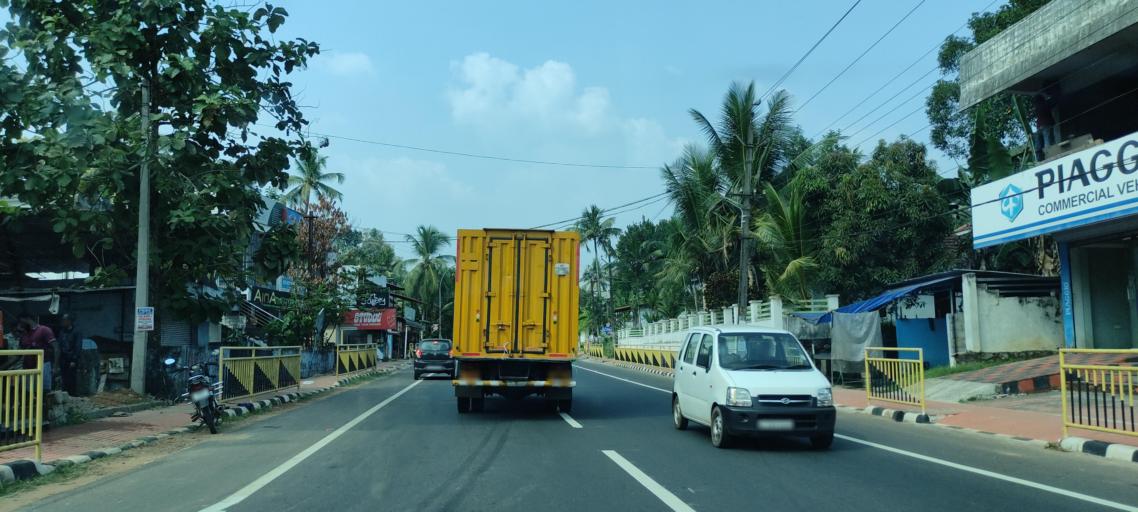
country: IN
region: Kerala
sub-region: Alappuzha
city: Chengannur
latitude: 9.2805
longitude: 76.6551
